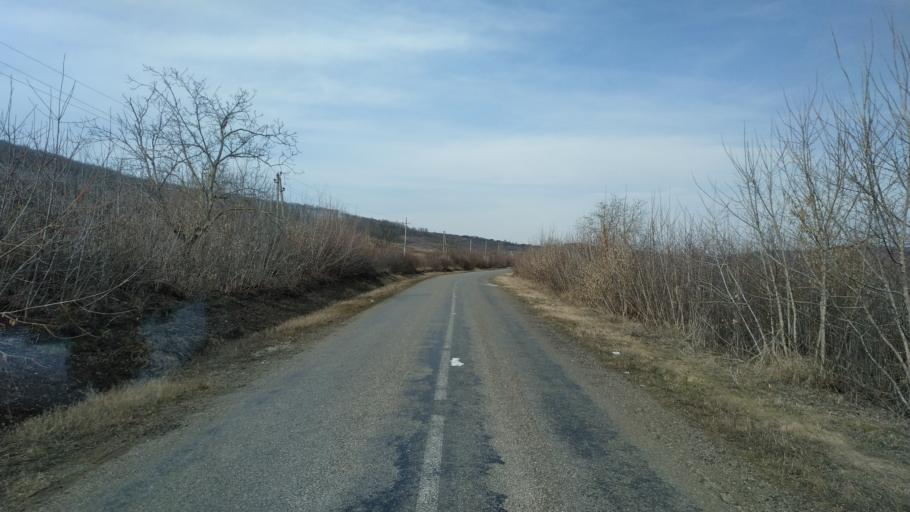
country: MD
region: Nisporeni
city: Nisporeni
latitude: 47.1791
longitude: 28.0811
